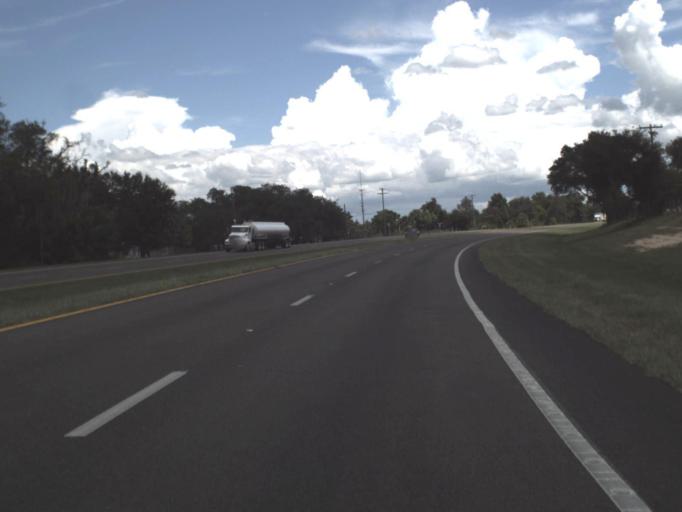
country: US
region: Florida
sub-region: Polk County
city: Wahneta
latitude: 27.9158
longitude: -81.7409
